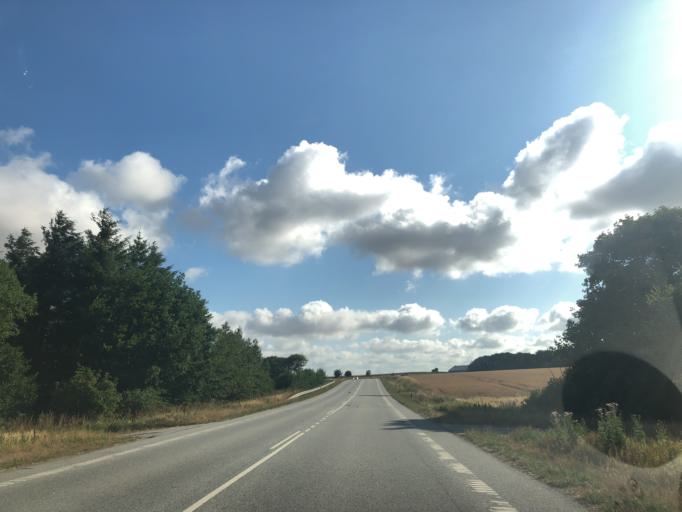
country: DK
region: Central Jutland
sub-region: Skive Kommune
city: Skive
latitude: 56.6324
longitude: 8.9156
